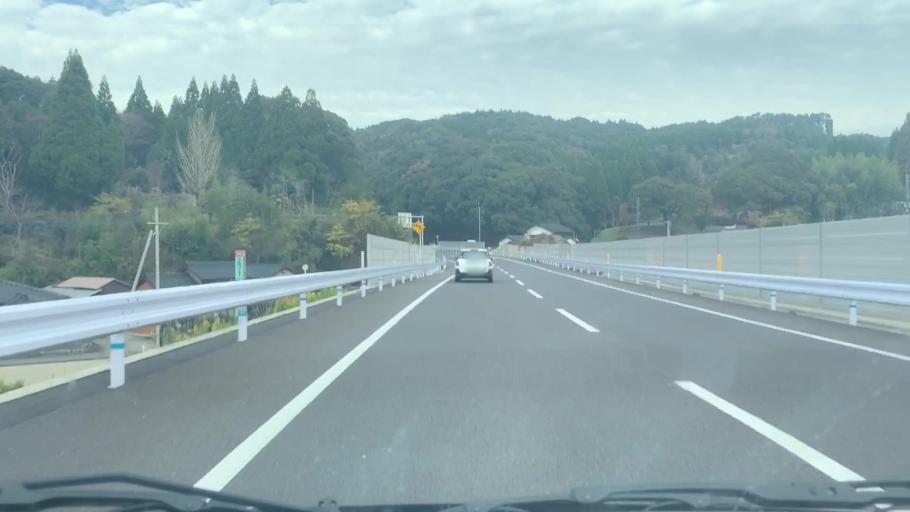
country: JP
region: Saga Prefecture
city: Takeocho-takeo
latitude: 33.2605
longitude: 129.9725
